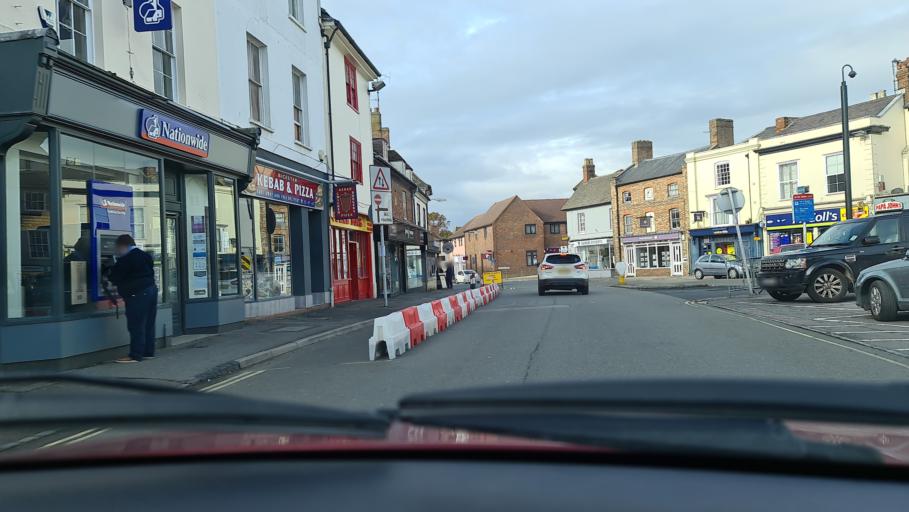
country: GB
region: England
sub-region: Oxfordshire
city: Bicester
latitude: 51.8967
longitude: -1.1509
